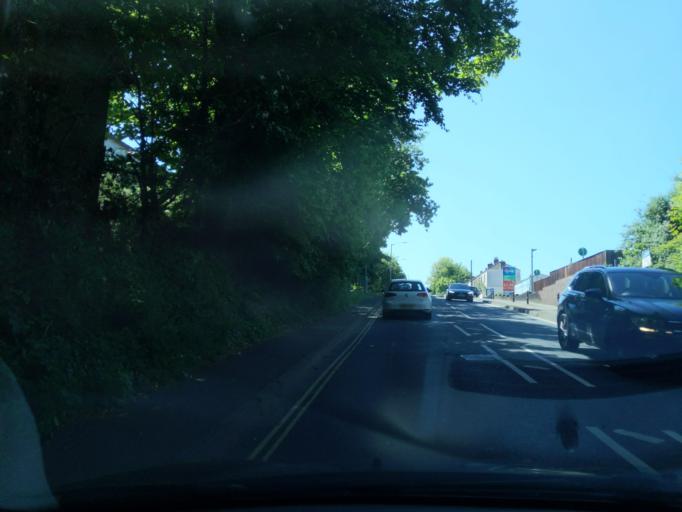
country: GB
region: England
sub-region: Cornwall
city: St Austell
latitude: 50.3387
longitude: -4.7667
